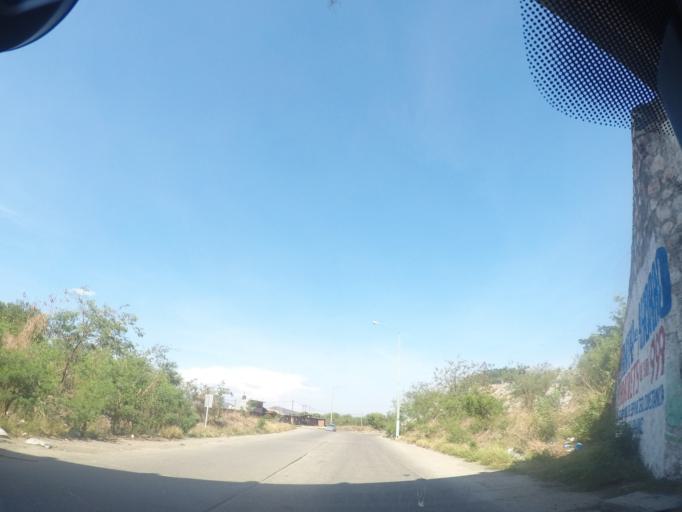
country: MX
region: Oaxaca
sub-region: Santo Domingo Tehuantepec
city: La Noria
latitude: 16.2217
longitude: -95.2073
